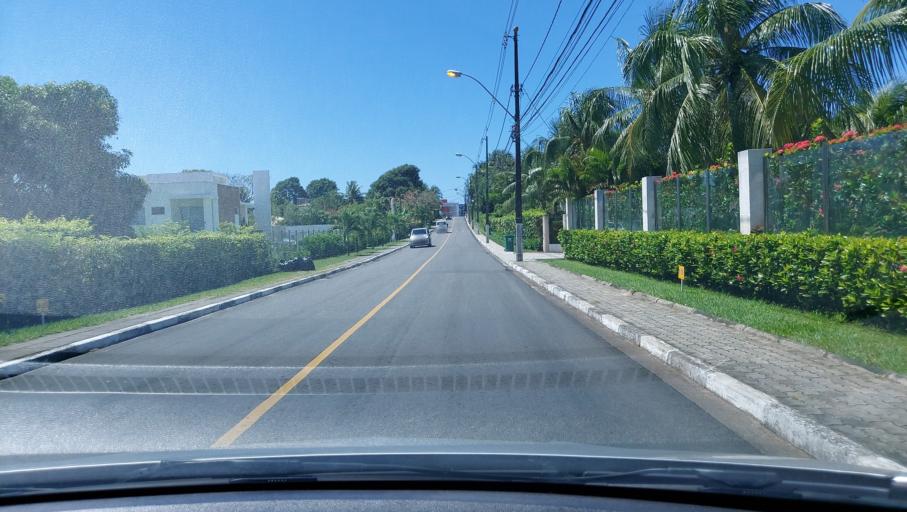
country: BR
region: Bahia
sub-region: Lauro De Freitas
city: Lauro de Freitas
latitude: -12.8710
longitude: -38.3064
